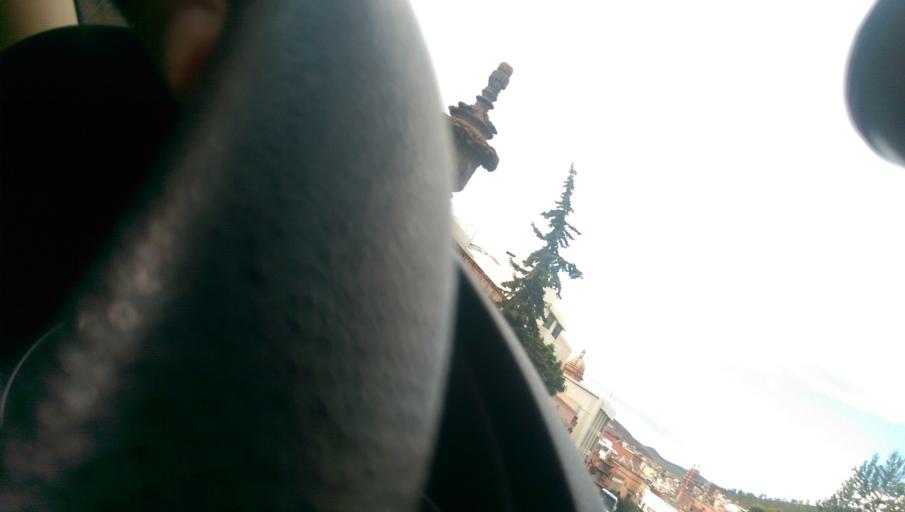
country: MX
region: Zacatecas
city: Zacatecas
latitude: 22.7706
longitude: -102.5754
